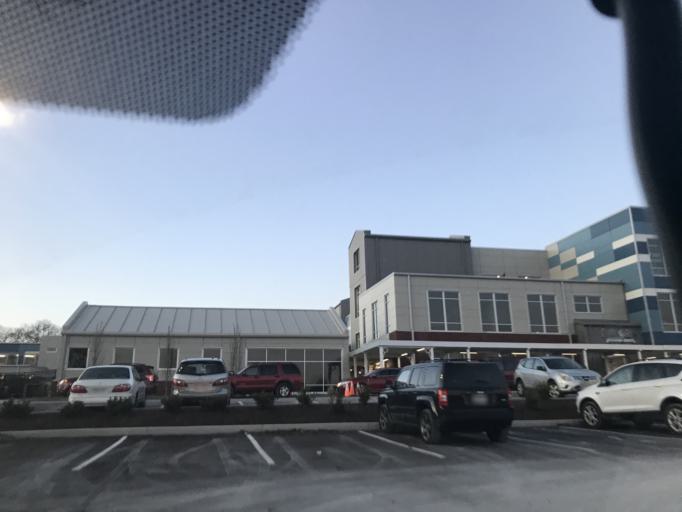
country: US
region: Tennessee
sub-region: Davidson County
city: Nashville
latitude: 36.1665
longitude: -86.7538
